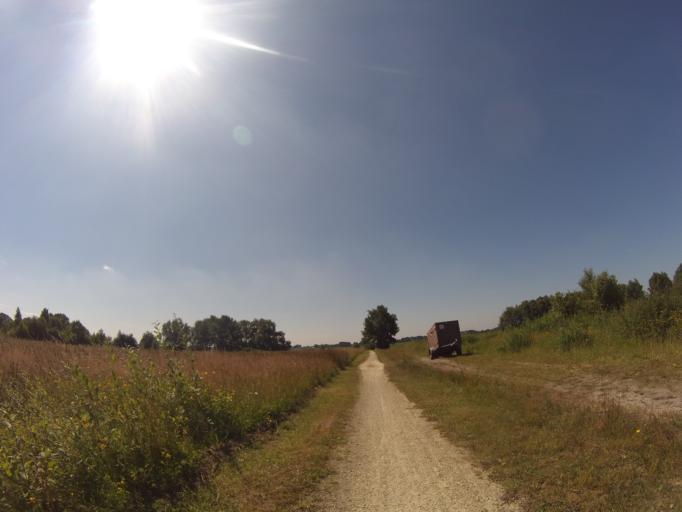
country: DE
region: Lower Saxony
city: Twist
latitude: 52.6574
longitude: 7.0118
